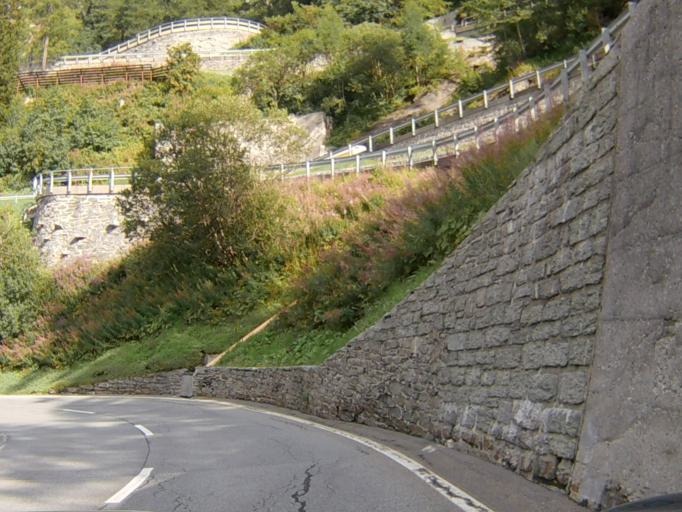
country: CH
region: Grisons
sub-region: Maloja District
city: Silvaplana
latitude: 46.3949
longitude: 9.6906
